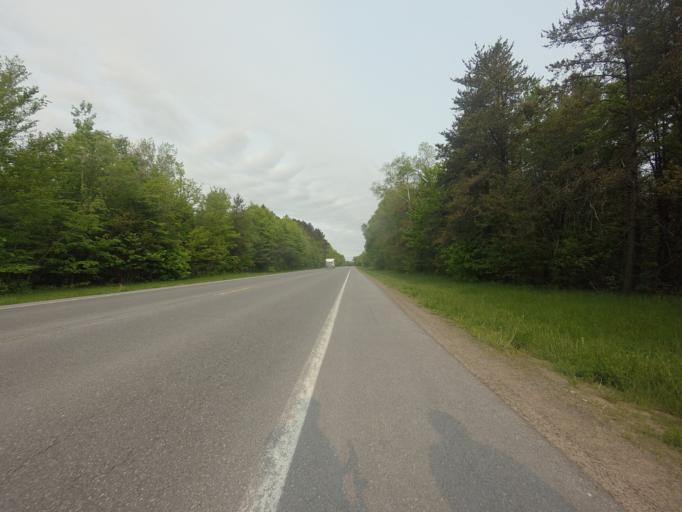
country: US
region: New York
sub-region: Jefferson County
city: Carthage
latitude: 44.0332
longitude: -75.6030
